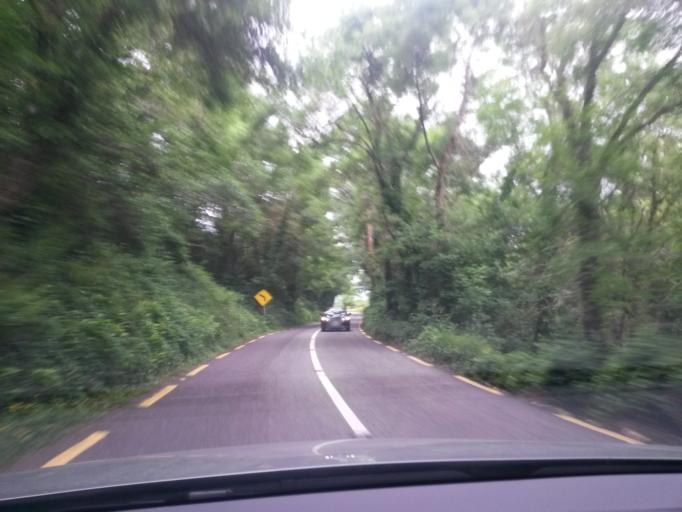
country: IE
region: Munster
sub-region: Ciarrai
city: Tralee
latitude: 52.2389
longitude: -9.6720
